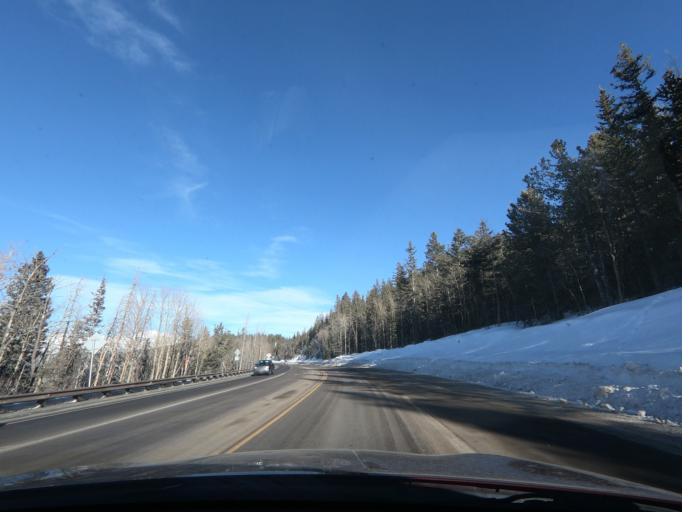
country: US
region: Colorado
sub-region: Teller County
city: Cripple Creek
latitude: 38.7621
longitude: -105.1590
